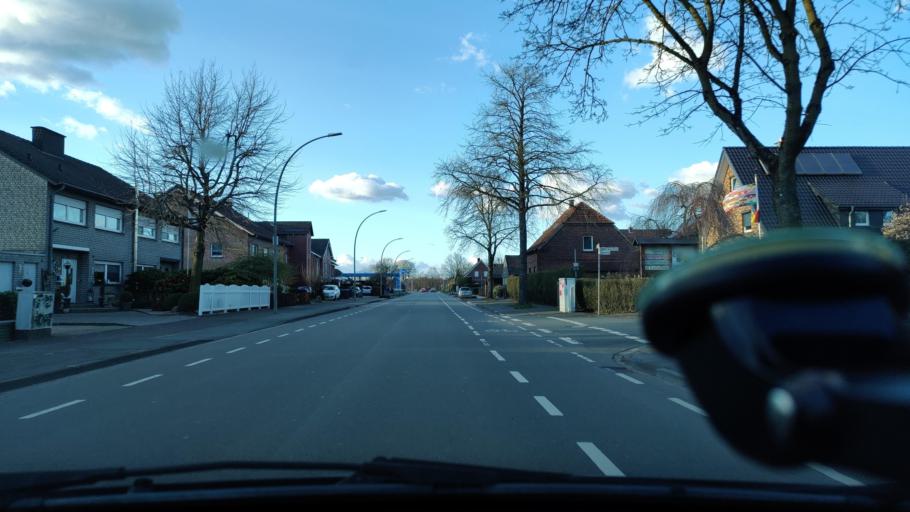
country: DE
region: North Rhine-Westphalia
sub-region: Regierungsbezirk Munster
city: Coesfeld
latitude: 51.9019
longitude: 7.1880
